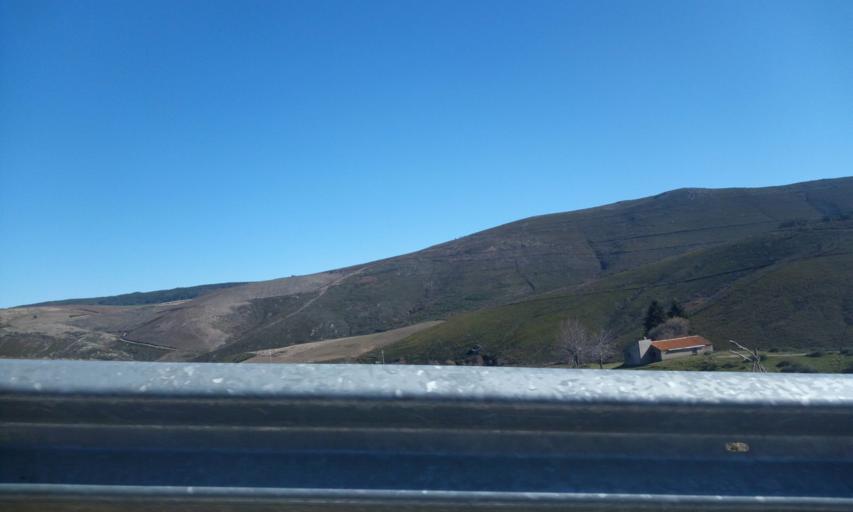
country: PT
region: Guarda
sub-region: Manteigas
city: Manteigas
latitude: 40.4540
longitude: -7.5103
